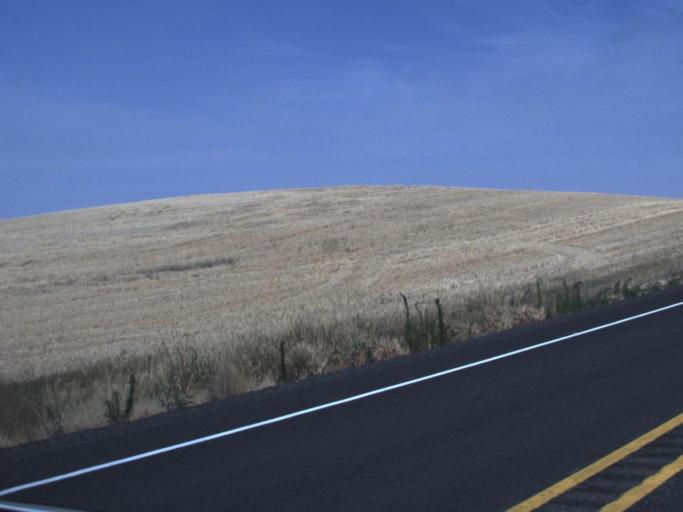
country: US
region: Washington
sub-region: Whitman County
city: Pullman
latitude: 46.8188
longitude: -117.1169
